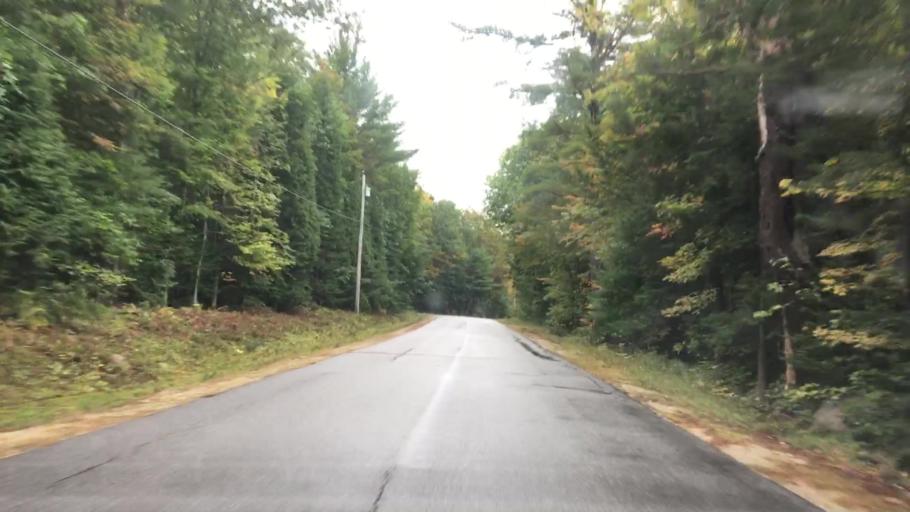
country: US
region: Maine
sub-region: Cumberland County
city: Harrison
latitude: 44.0384
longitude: -70.6072
